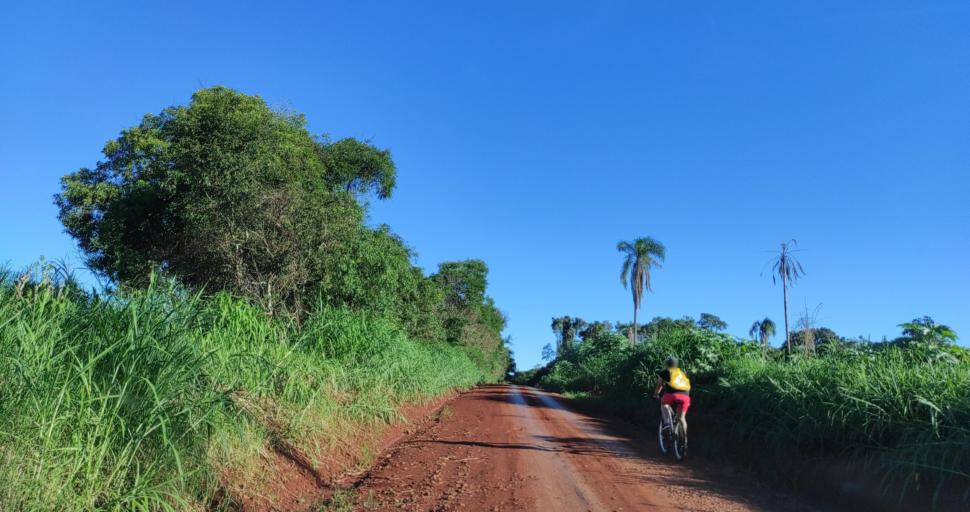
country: AR
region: Misiones
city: Puerto Rico
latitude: -26.8307
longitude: -55.0117
